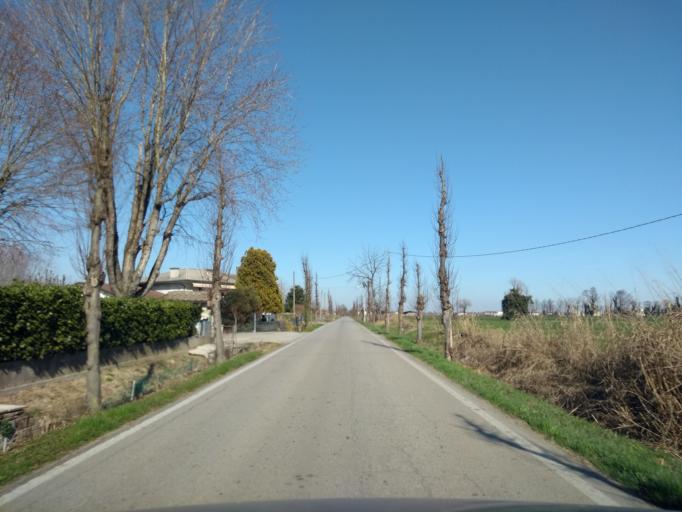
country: IT
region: Veneto
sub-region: Provincia di Padova
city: San Pietro in Gu
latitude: 45.6158
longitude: 11.6521
